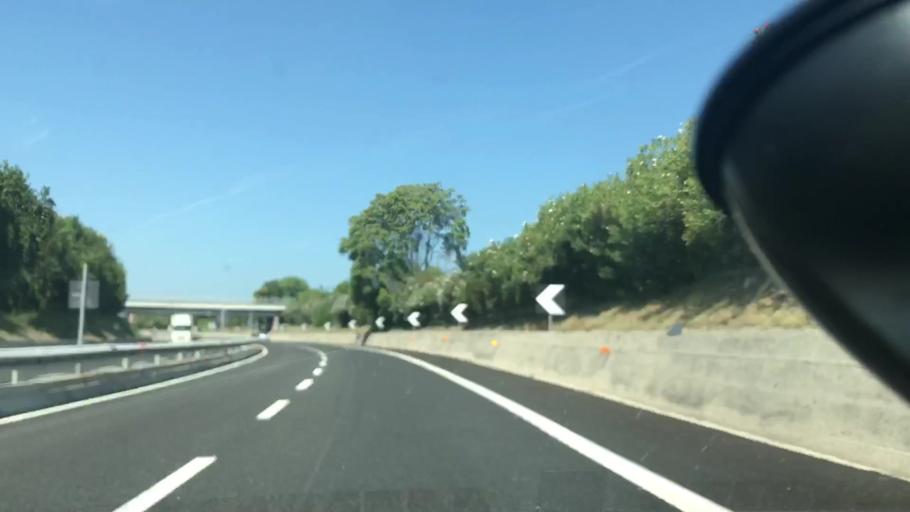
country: IT
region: Abruzzo
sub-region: Provincia di Chieti
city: Tollo
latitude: 42.3567
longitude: 14.3507
